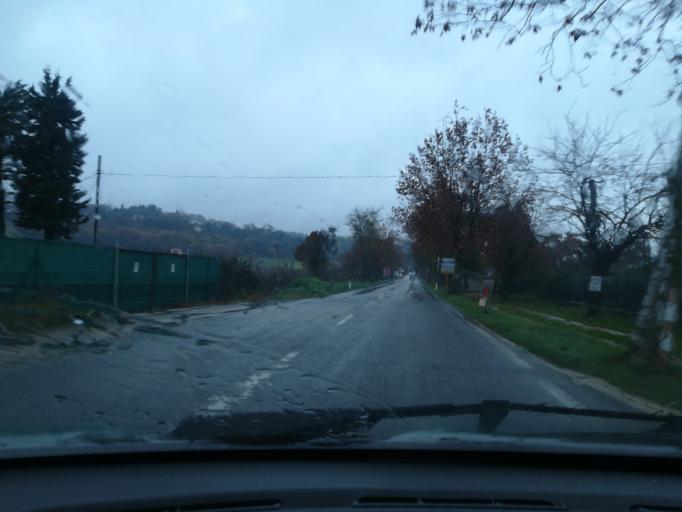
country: IT
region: The Marches
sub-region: Provincia di Macerata
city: Sforzacosta
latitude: 43.2678
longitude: 13.4236
